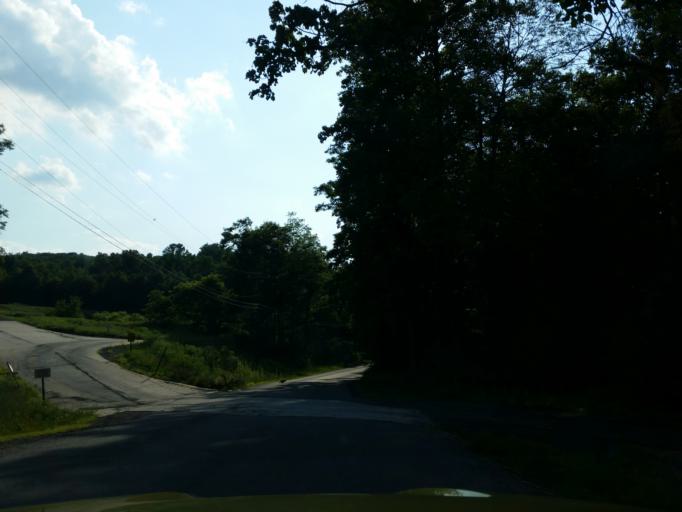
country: US
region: Pennsylvania
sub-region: Dauphin County
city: Williamstown
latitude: 40.4442
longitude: -76.6114
